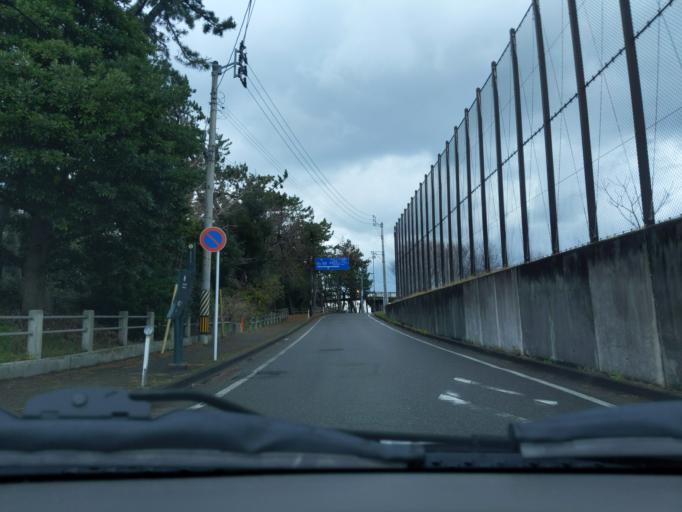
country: JP
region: Niigata
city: Niigata-shi
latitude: 37.9288
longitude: 139.0378
